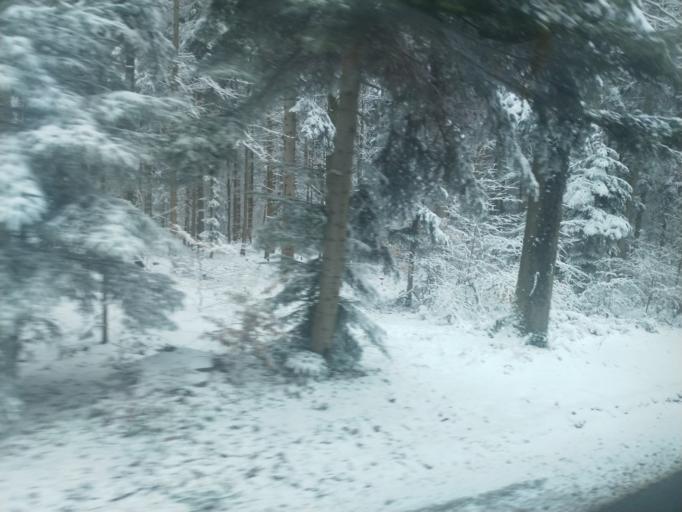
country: DE
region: Baden-Wuerttemberg
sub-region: Karlsruhe Region
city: Neuenburg
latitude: 48.8489
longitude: 8.5779
